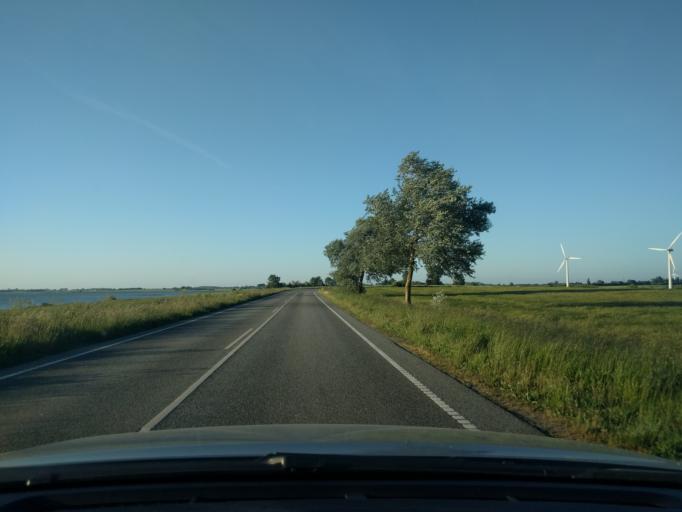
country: DK
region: South Denmark
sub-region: Kerteminde Kommune
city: Kerteminde
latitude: 55.4816
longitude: 10.6179
